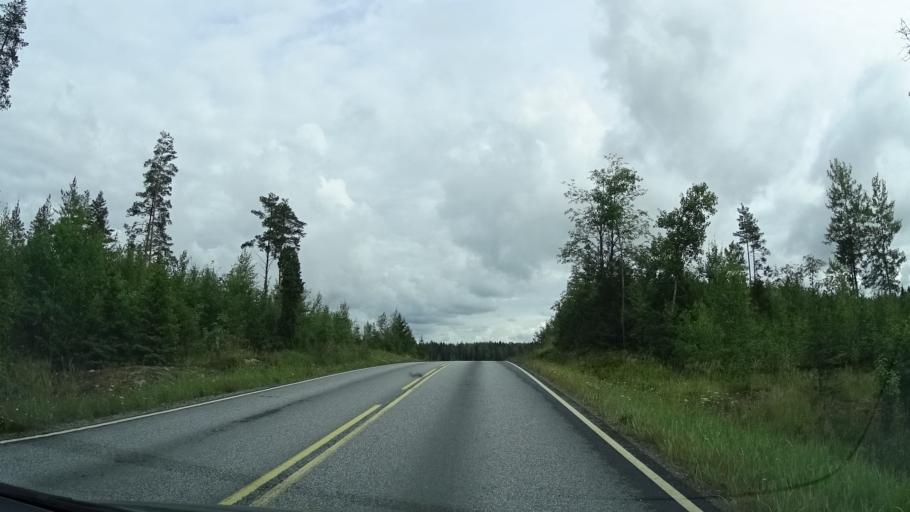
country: FI
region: Haeme
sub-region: Forssa
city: Humppila
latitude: 61.0964
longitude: 23.3547
